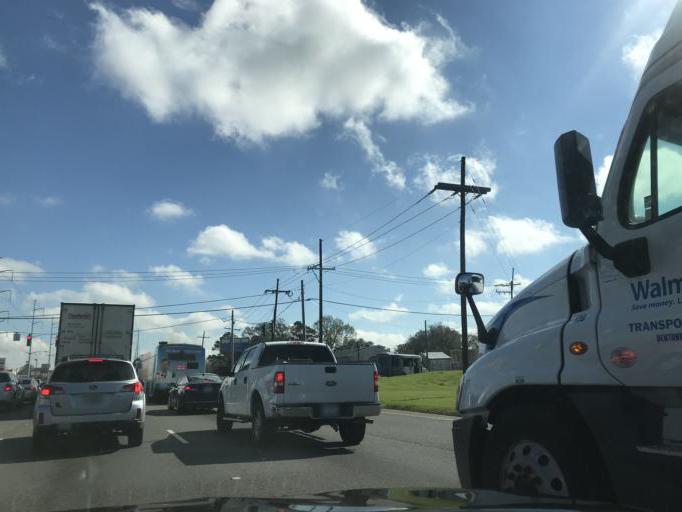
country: US
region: Louisiana
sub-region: Jefferson Parish
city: Metairie Terrace
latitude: 29.9753
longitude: -90.1752
